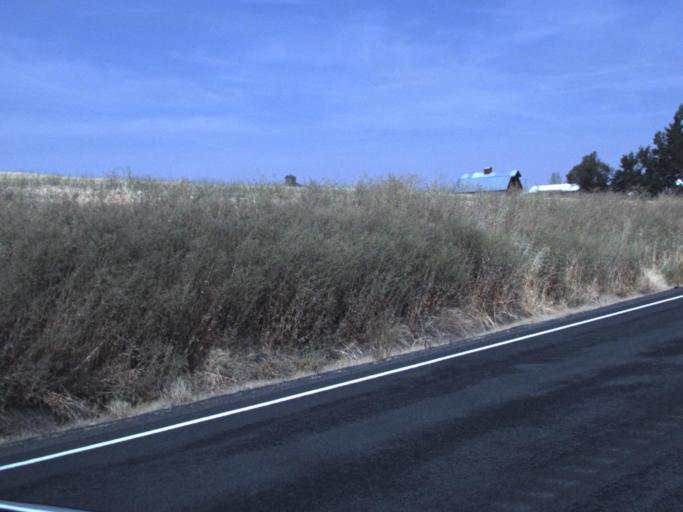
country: US
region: Washington
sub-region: Whitman County
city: Pullman
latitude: 46.8742
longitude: -117.1270
